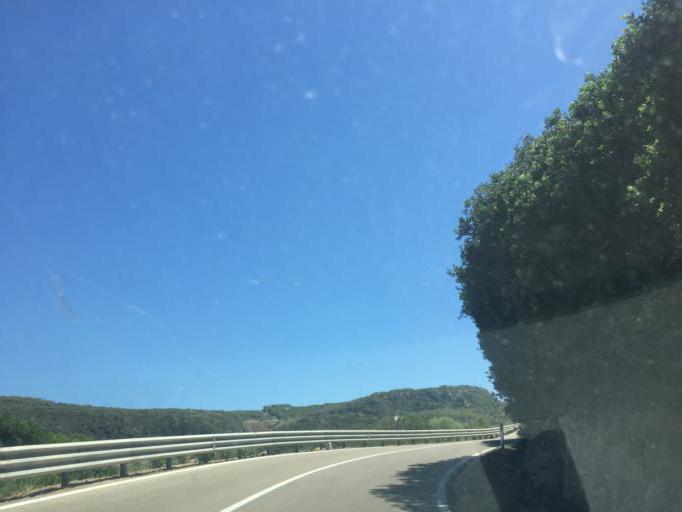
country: IT
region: Sardinia
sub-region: Provincia di Sassari
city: Castelsardo
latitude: 40.9100
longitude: 8.7371
